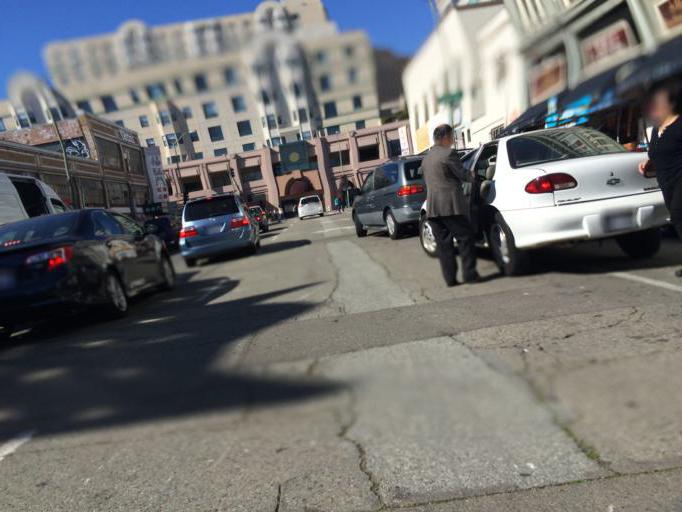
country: US
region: California
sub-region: Alameda County
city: Oakland
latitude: 37.8004
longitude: -122.2698
